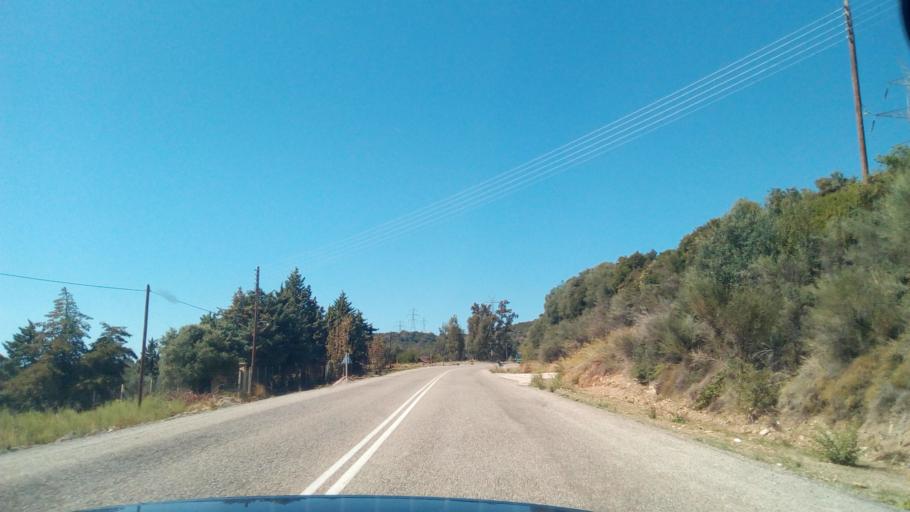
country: GR
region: West Greece
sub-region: Nomos Achaias
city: Kamarai
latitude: 38.4030
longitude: 21.9875
